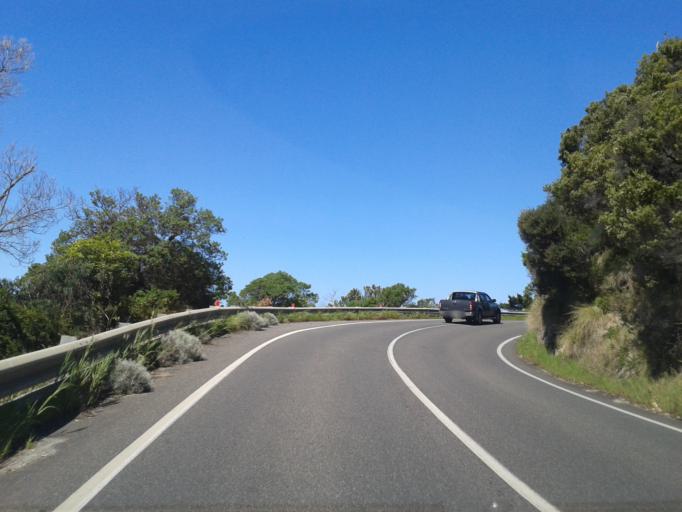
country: AU
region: Victoria
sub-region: Surf Coast
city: Anglesea
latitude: -38.5797
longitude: 143.9450
